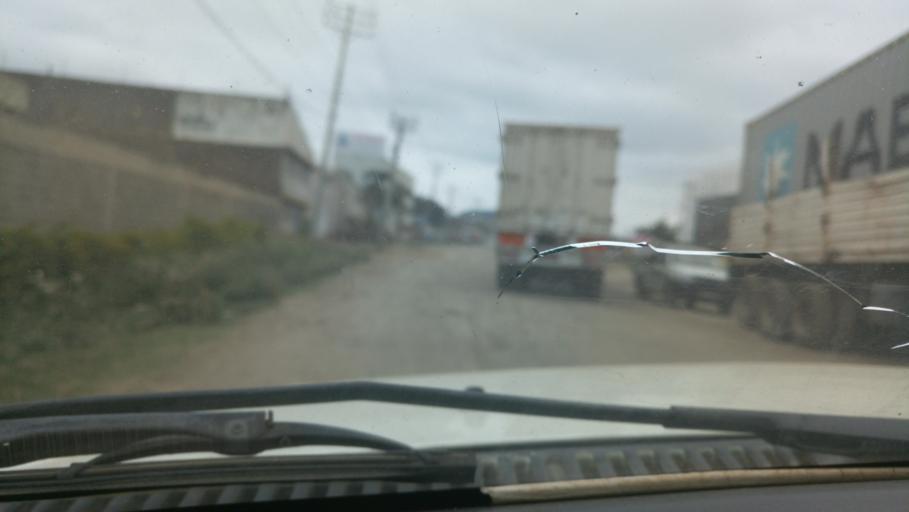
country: KE
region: Nairobi Area
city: Pumwani
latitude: -1.3329
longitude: 36.8659
